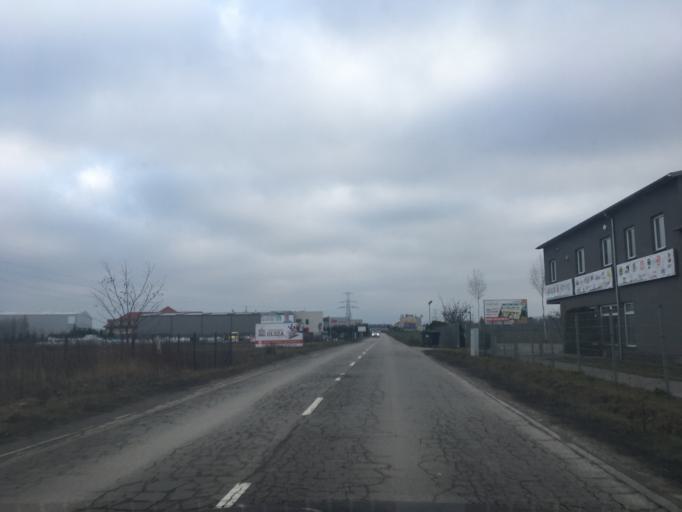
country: PL
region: Masovian Voivodeship
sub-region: Powiat piaseczynski
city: Lesznowola
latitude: 52.0859
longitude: 20.9694
